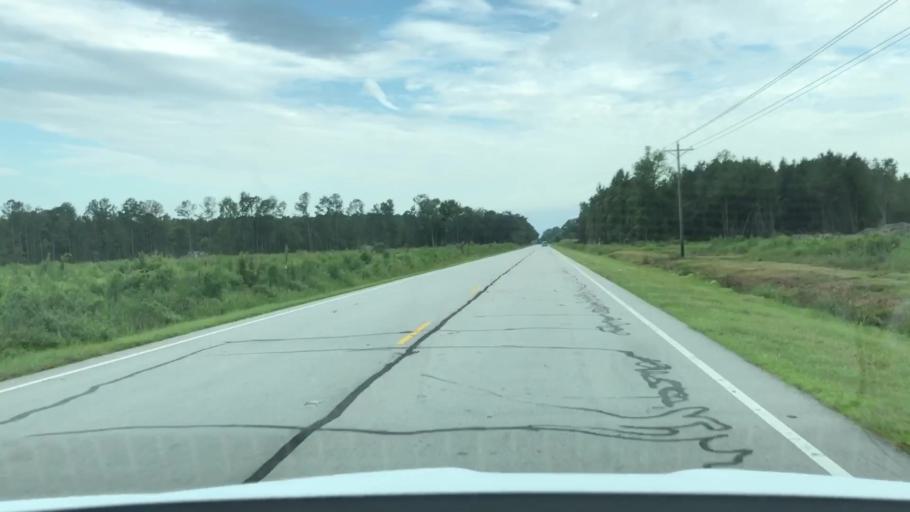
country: US
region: North Carolina
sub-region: Lenoir County
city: Kinston
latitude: 35.1287
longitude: -77.5227
